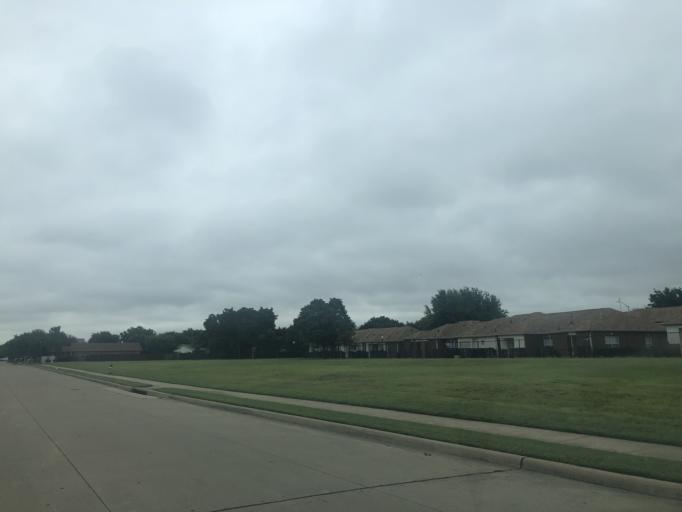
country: US
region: Texas
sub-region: Dallas County
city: Dallas
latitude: 32.7880
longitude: -96.8631
